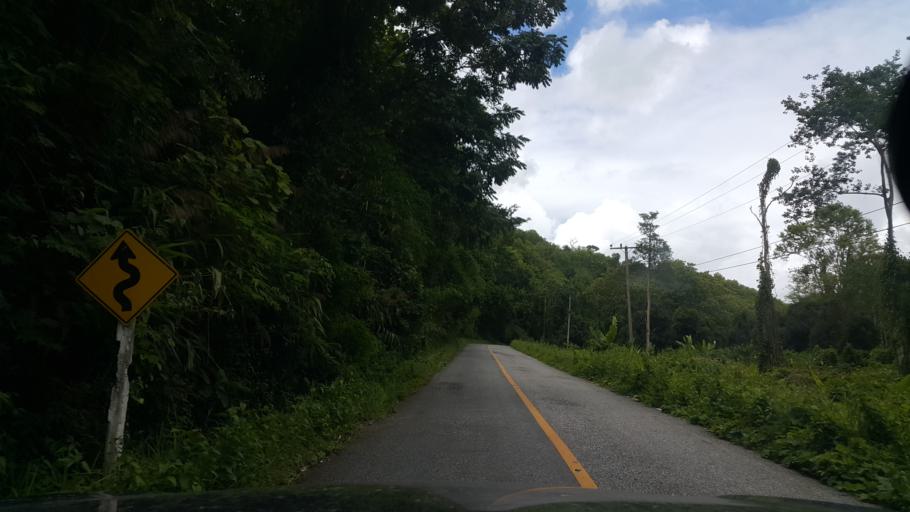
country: TH
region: Loei
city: Na Haeo
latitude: 17.6362
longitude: 100.9017
